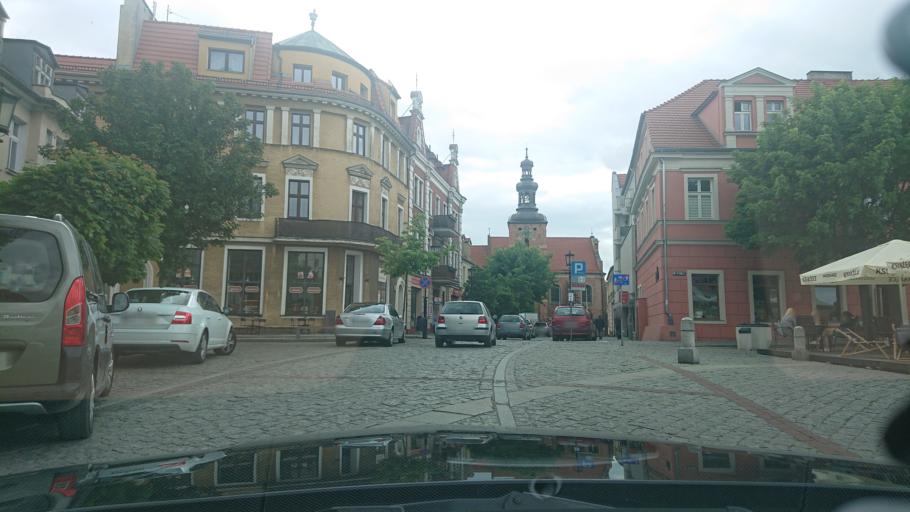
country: PL
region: Greater Poland Voivodeship
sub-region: Powiat gnieznienski
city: Gniezno
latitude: 52.5357
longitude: 17.5962
